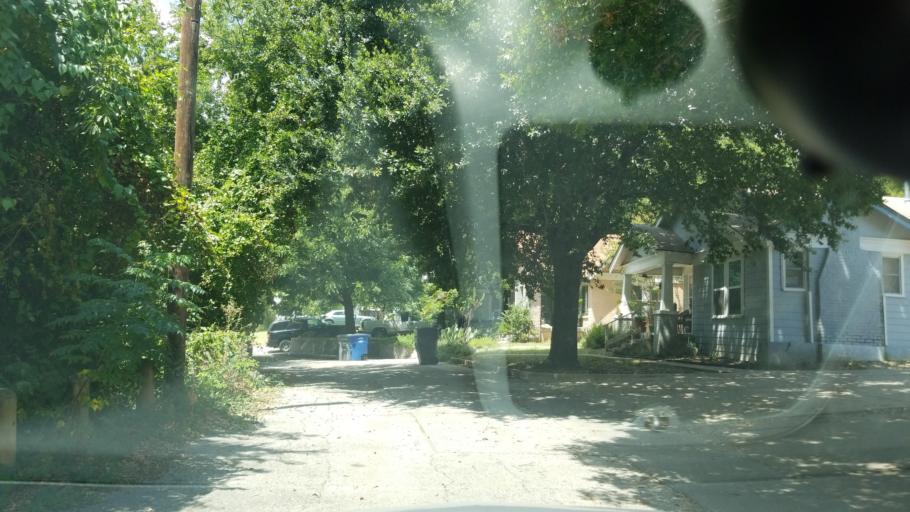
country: US
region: Texas
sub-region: Dallas County
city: Cockrell Hill
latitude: 32.7319
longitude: -96.8421
